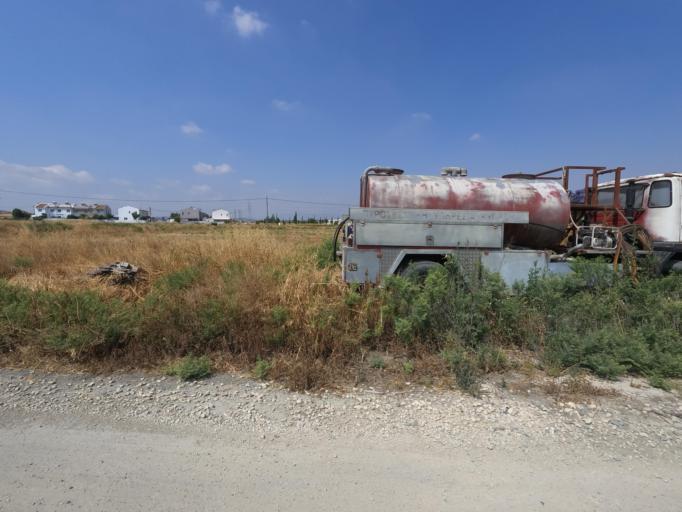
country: CY
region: Lefkosia
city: Dali
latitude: 35.0385
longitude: 33.4396
